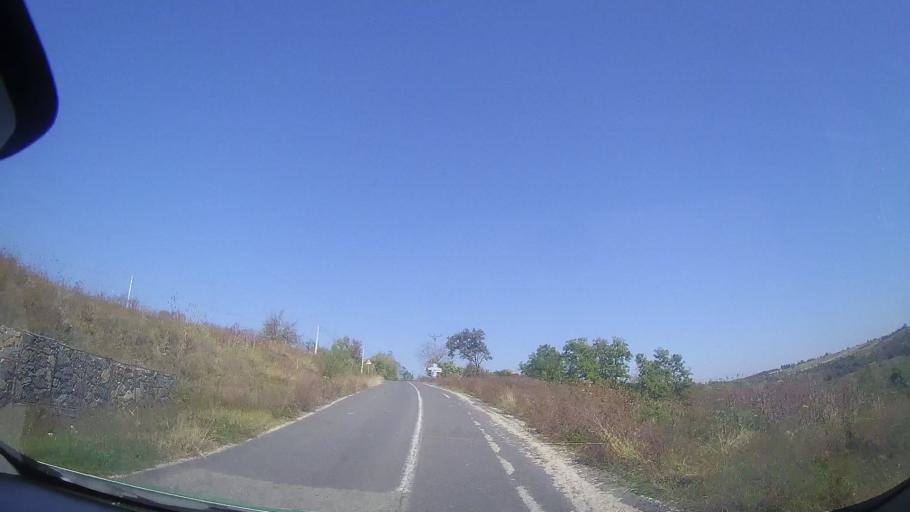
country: RO
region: Timis
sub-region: Comuna Ohaba Lunga
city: Ohaba Lunga
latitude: 45.9028
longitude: 21.9358
